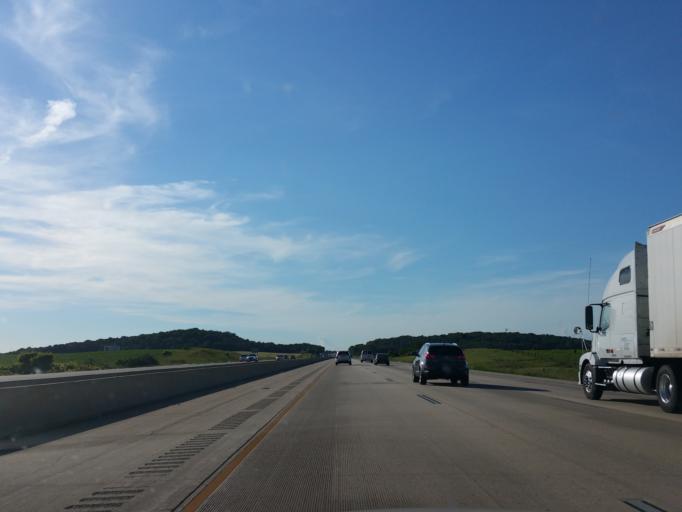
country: US
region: Wisconsin
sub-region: Columbia County
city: Poynette
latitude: 43.3055
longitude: -89.4296
